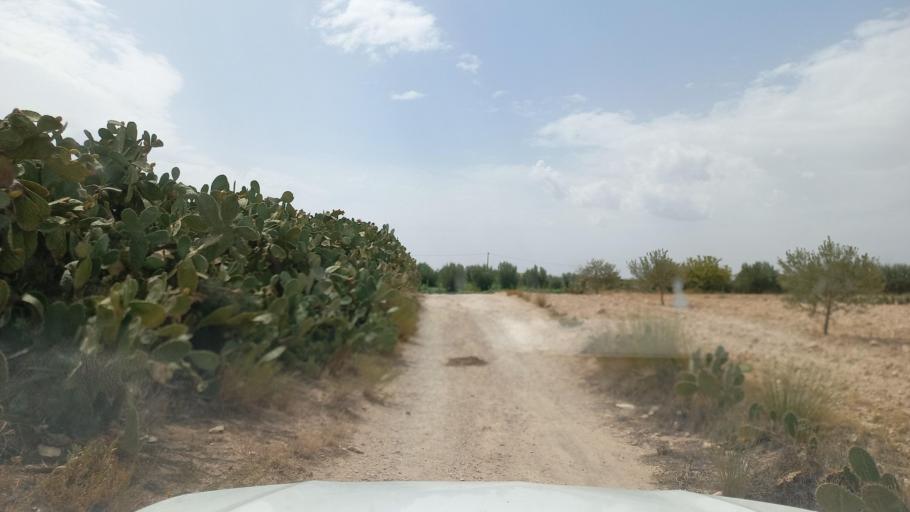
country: TN
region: Al Qasrayn
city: Kasserine
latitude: 35.2730
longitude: 9.0232
